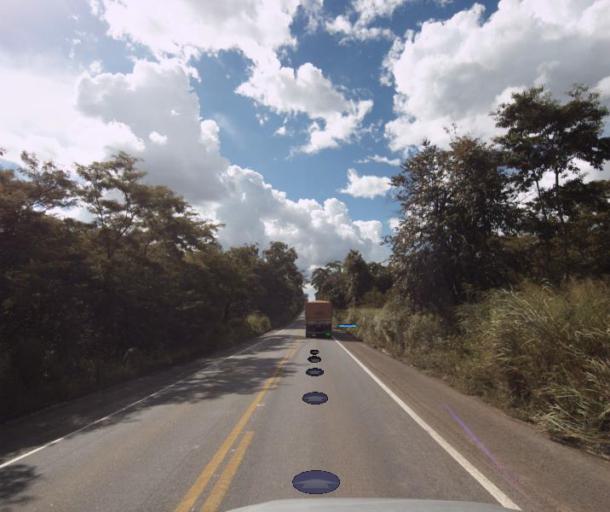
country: BR
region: Goias
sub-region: Porangatu
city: Porangatu
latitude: -13.2487
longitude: -49.1392
